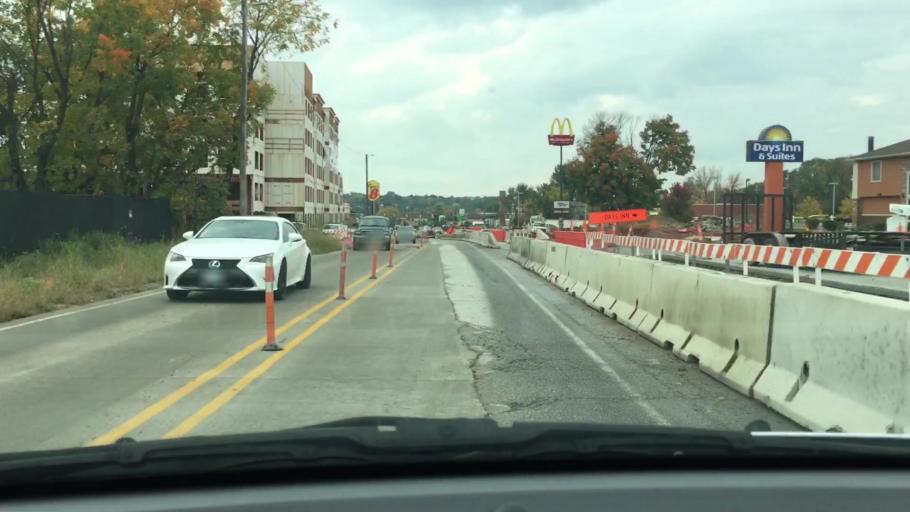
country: US
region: Iowa
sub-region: Johnson County
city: Coralville
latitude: 41.6797
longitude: -91.5658
